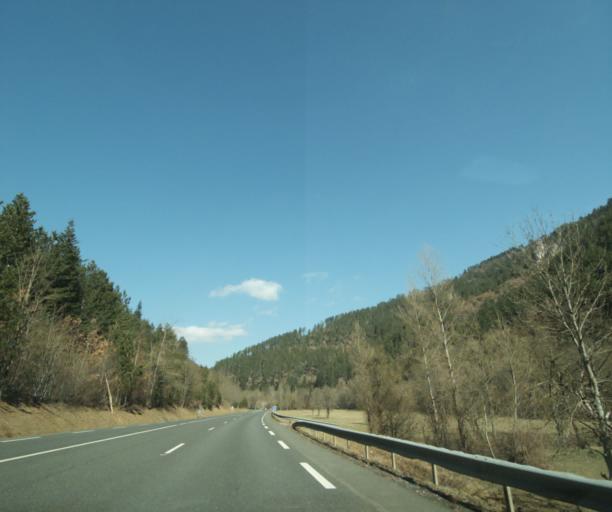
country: FR
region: Languedoc-Roussillon
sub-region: Departement de la Lozere
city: Mende
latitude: 44.4988
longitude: 3.4625
